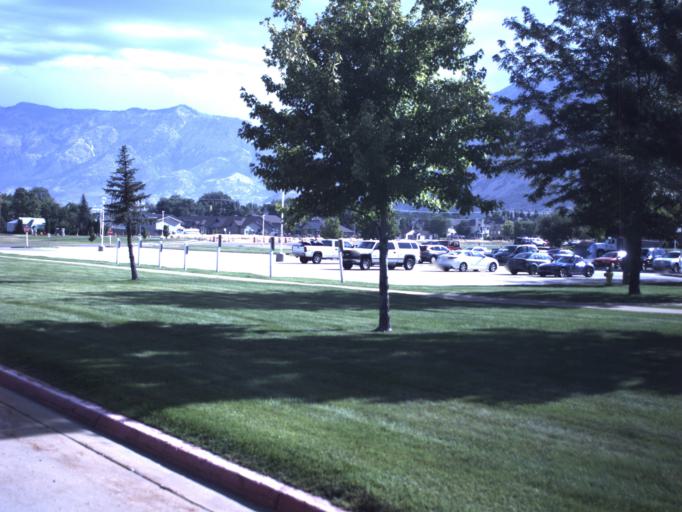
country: US
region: Utah
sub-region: Weber County
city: Harrisville
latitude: 41.2644
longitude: -111.9665
